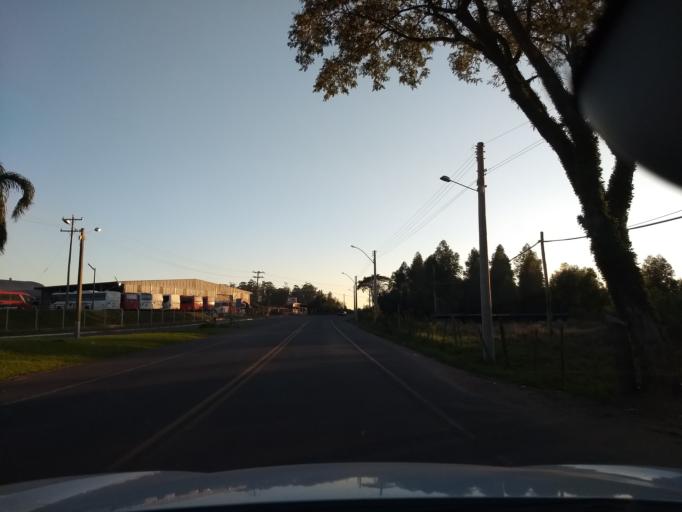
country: BR
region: Rio Grande do Sul
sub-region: Santa Cruz Do Sul
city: Santa Cruz do Sul
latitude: -29.7200
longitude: -52.5166
